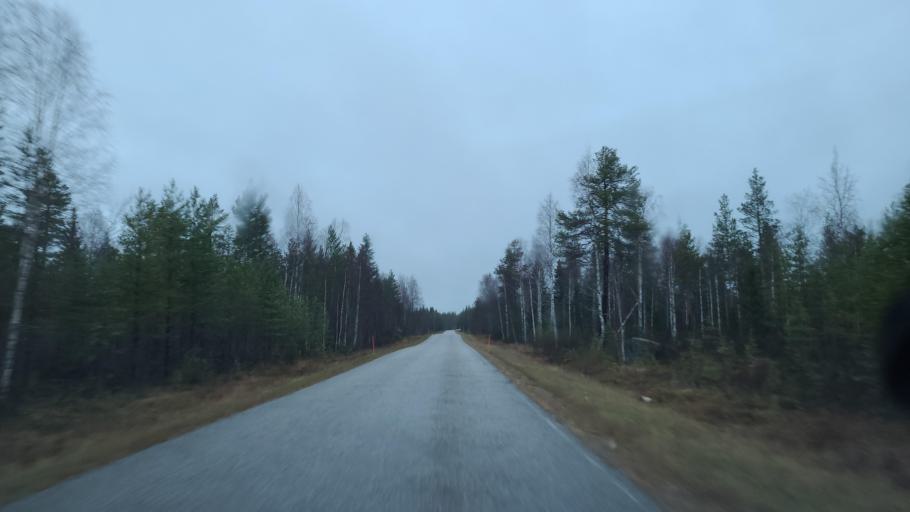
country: FI
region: Lapland
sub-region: Kemi-Tornio
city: Simo
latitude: 65.8980
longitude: 25.2097
